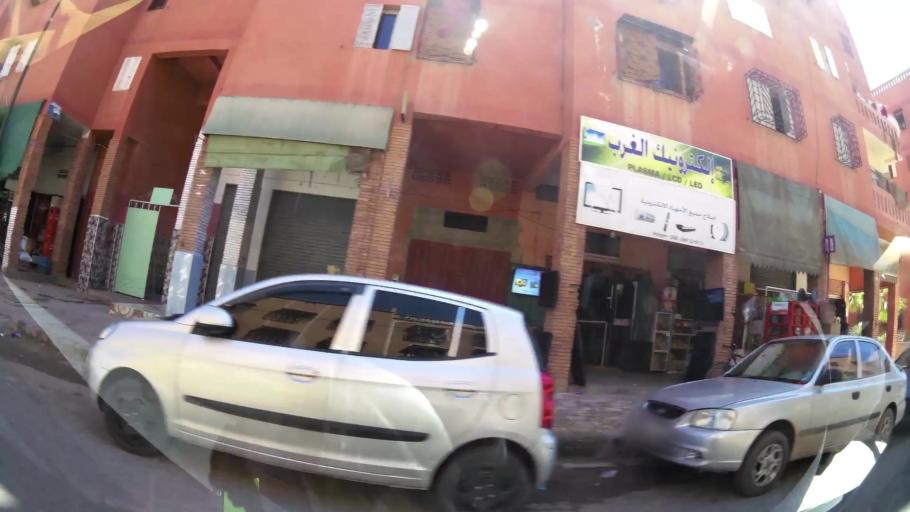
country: MA
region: Marrakech-Tensift-Al Haouz
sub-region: Marrakech
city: Marrakesh
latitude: 31.6359
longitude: -8.0636
